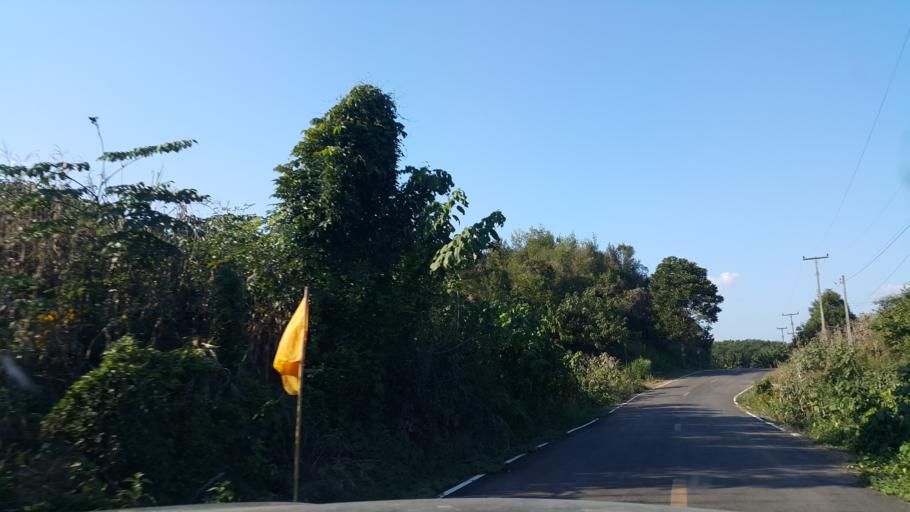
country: TH
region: Sukhothai
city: Thung Saliam
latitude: 17.4037
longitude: 99.5129
